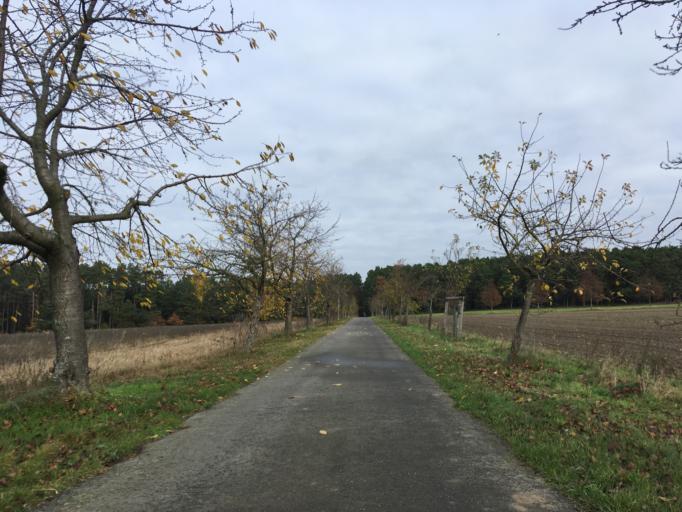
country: DE
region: Brandenburg
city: Tauer
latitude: 51.9015
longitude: 14.4595
